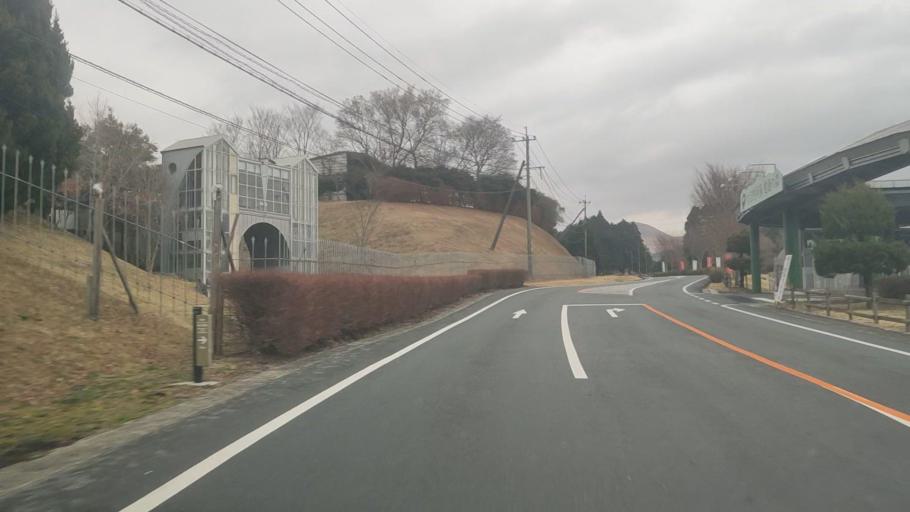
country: JP
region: Kumamoto
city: Aso
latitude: 32.8943
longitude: 131.0034
